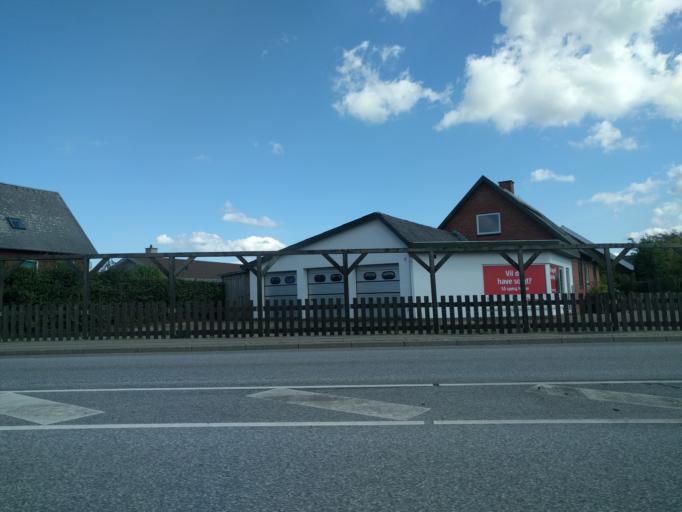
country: DK
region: Central Jutland
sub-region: Skive Kommune
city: Skive
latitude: 56.5901
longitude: 9.0290
